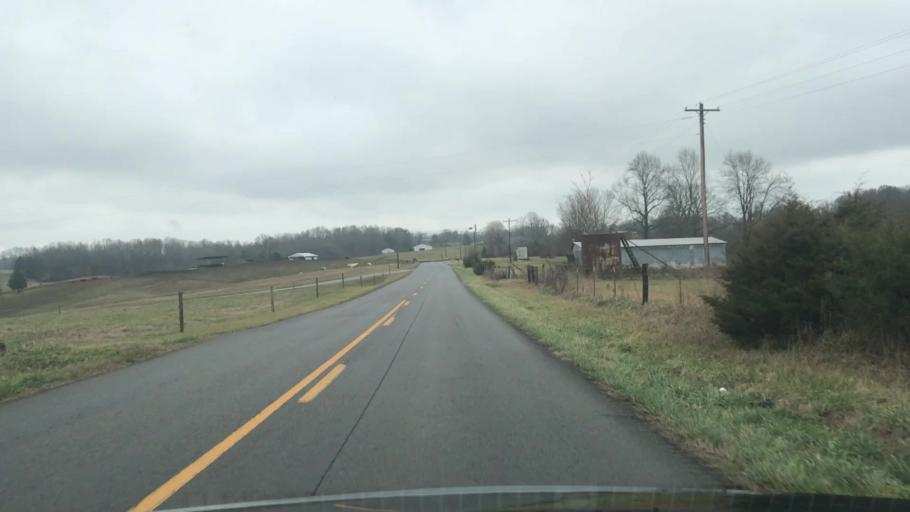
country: US
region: Kentucky
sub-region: Monroe County
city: Tompkinsville
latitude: 36.7930
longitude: -85.7379
